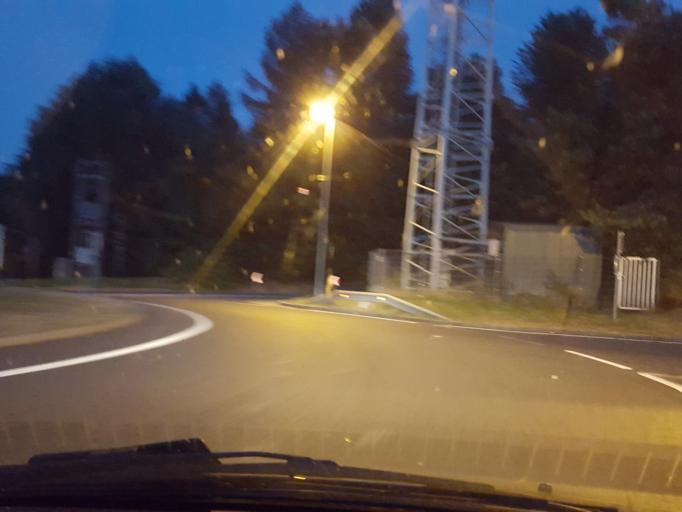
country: AT
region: Lower Austria
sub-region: Politischer Bezirk Melk
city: Ybbs an der Donau
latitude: 48.1584
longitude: 15.1137
